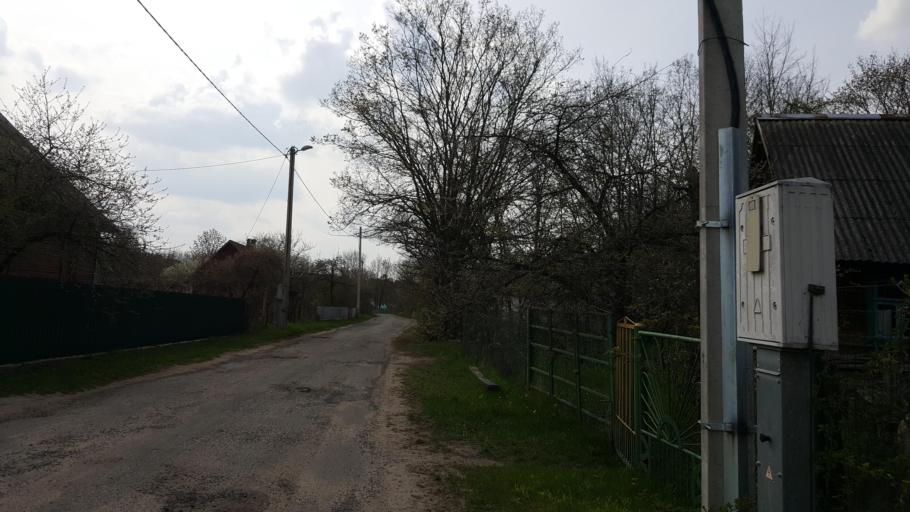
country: BY
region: Brest
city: Zhabinka
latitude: 52.2198
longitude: 23.9228
